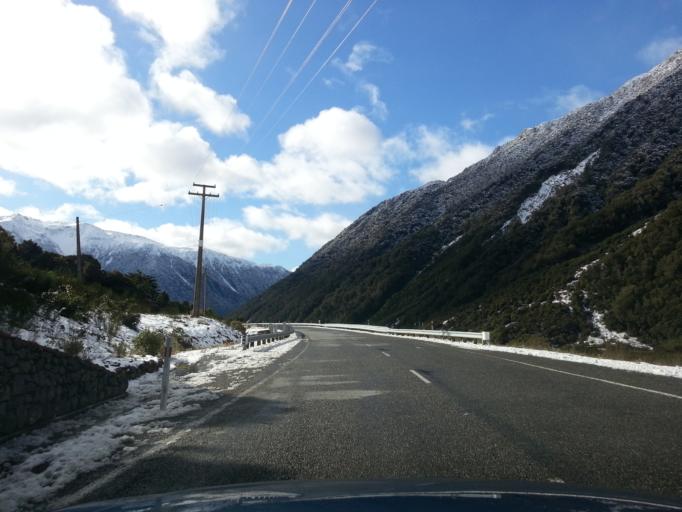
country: NZ
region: West Coast
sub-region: Grey District
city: Greymouth
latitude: -42.8376
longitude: 171.5621
